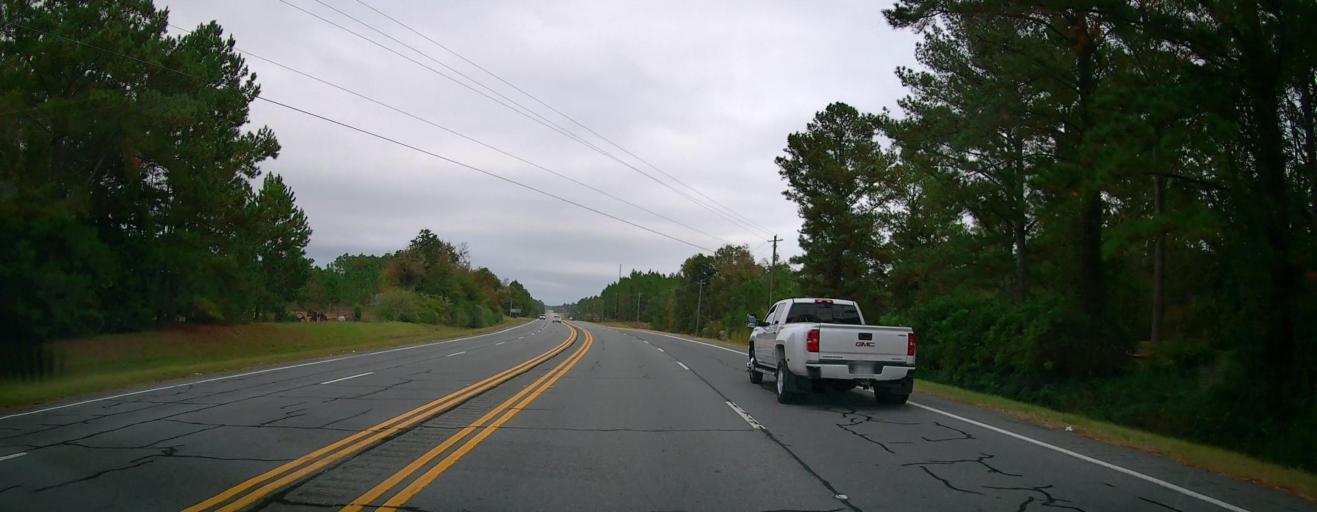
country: US
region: Georgia
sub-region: Tift County
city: Omega
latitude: 31.3072
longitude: -83.6379
